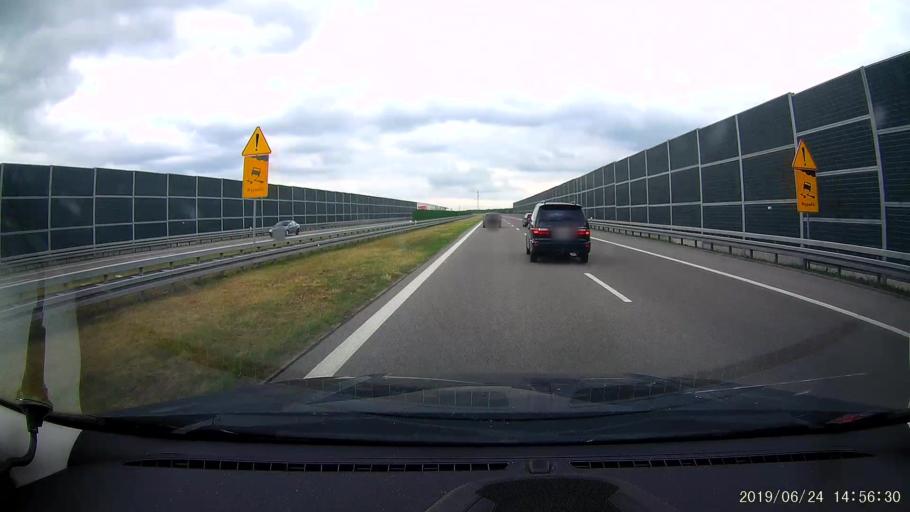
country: PL
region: Subcarpathian Voivodeship
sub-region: Powiat ropczycko-sedziszowski
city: Sedziszow Malopolski
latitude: 50.1128
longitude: 21.7408
